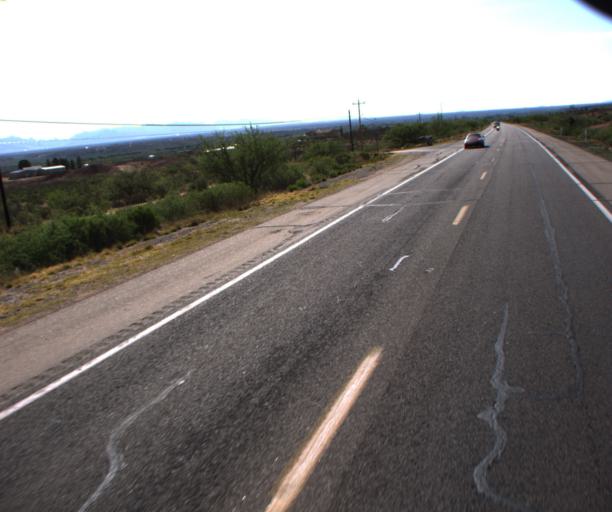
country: US
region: Arizona
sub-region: Cochise County
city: Benson
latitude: 31.9274
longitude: -110.2774
